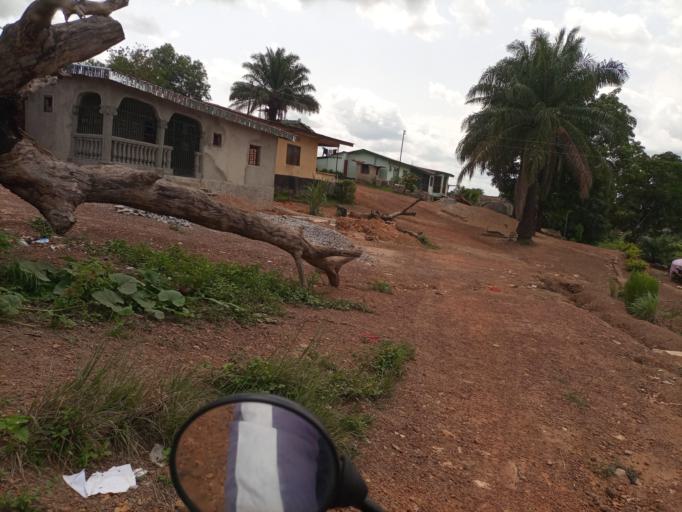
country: SL
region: Southern Province
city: Bo
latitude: 7.9520
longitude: -11.7372
